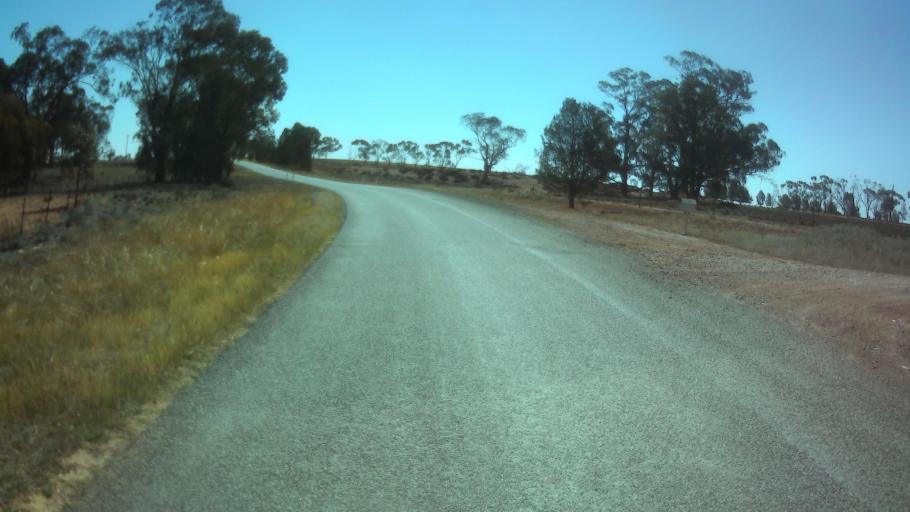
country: AU
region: New South Wales
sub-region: Weddin
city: Grenfell
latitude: -33.7532
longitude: 147.8426
